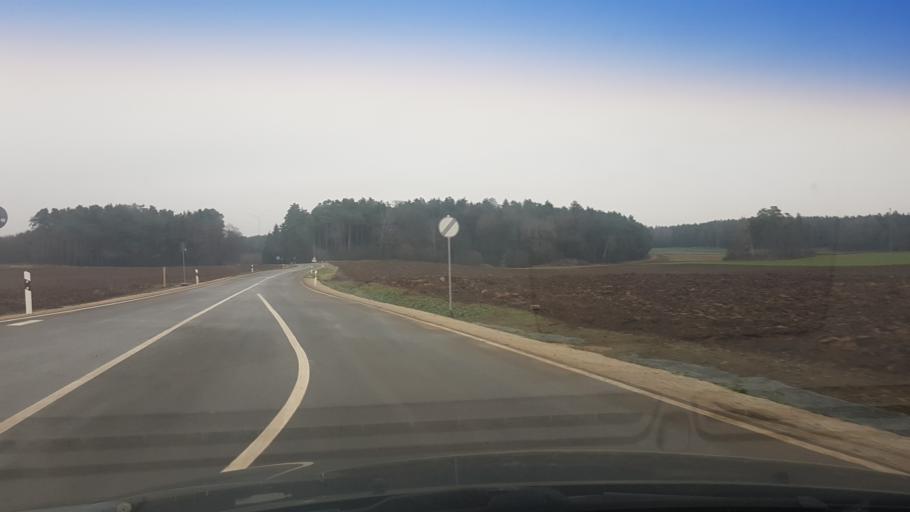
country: DE
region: Bavaria
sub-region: Upper Franconia
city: Wonsees
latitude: 50.0240
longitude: 11.2676
